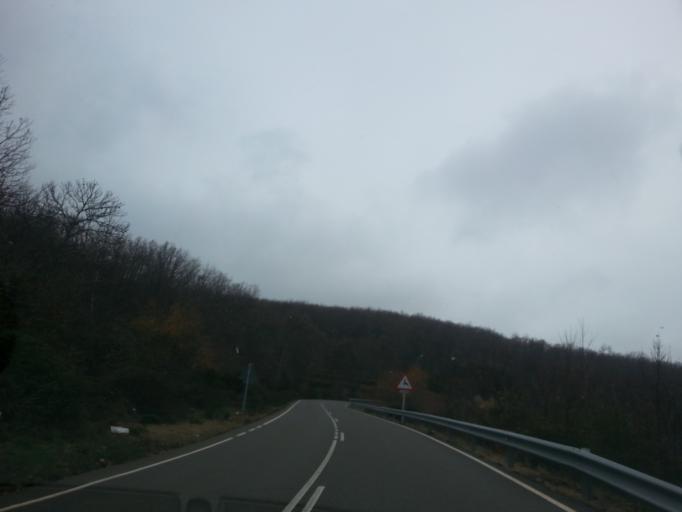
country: ES
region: Castille and Leon
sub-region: Provincia de Salamanca
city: Madronal
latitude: 40.4711
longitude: -6.0796
